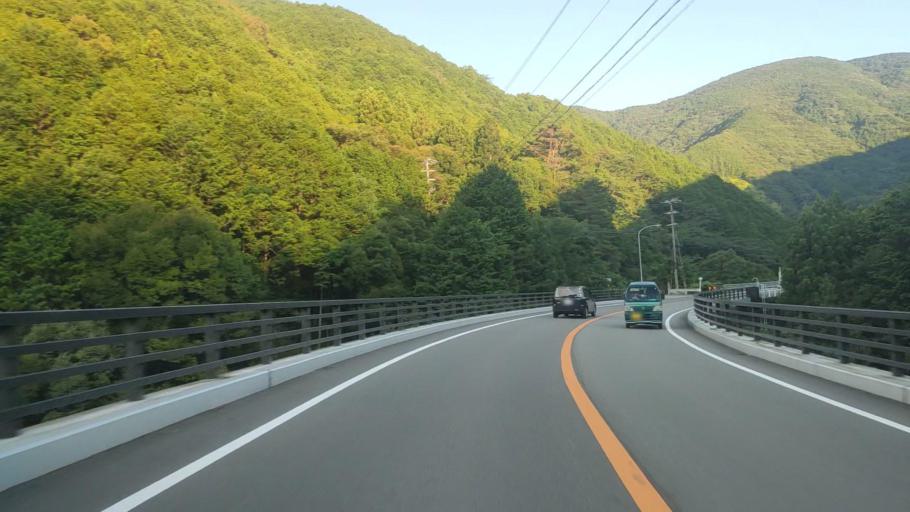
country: JP
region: Wakayama
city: Tanabe
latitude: 33.8167
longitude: 135.5612
